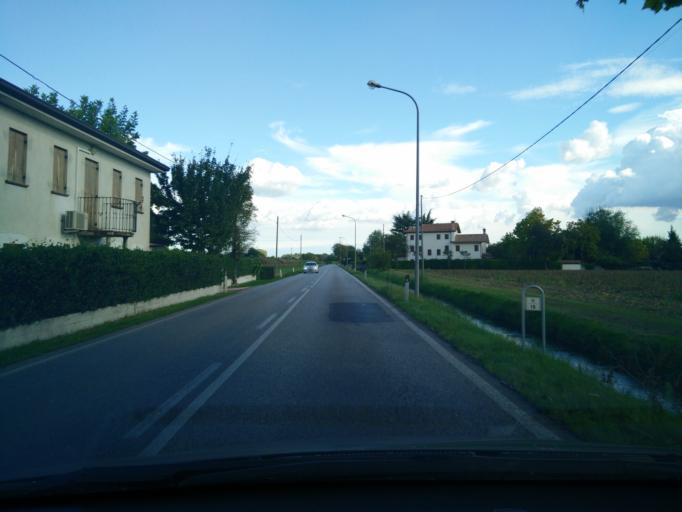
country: IT
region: Veneto
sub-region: Provincia di Treviso
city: Breda
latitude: 45.7445
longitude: 12.3414
